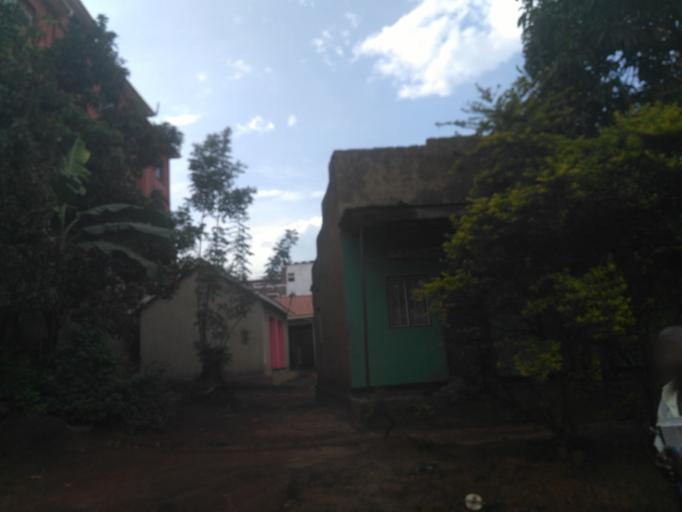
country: UG
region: Central Region
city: Kampala Central Division
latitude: 0.3595
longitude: 32.5850
